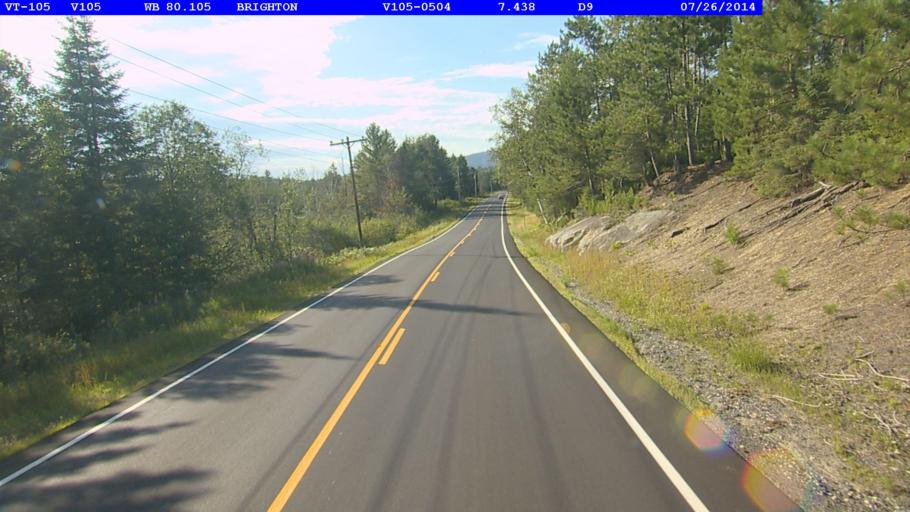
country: US
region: Vermont
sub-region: Caledonia County
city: Lyndonville
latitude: 44.7936
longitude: -71.8359
